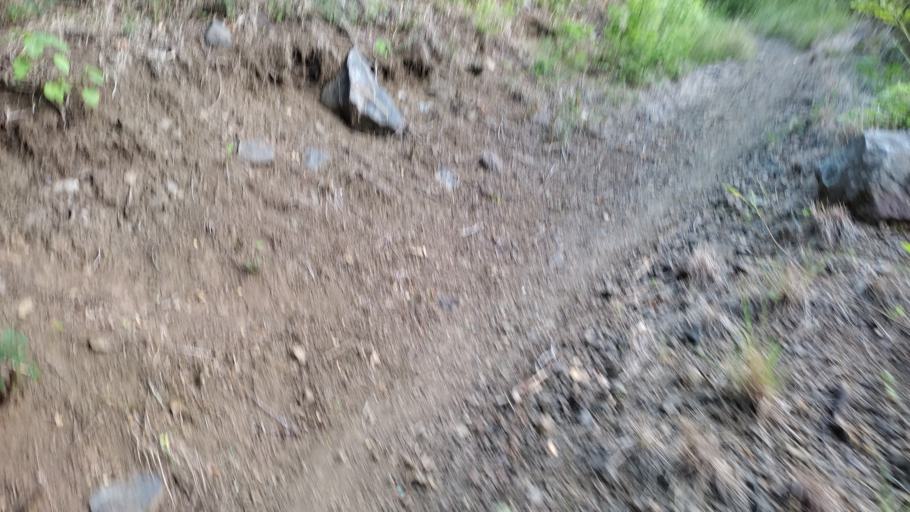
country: CO
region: Narino
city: Taminango
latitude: 1.5456
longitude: -77.3681
